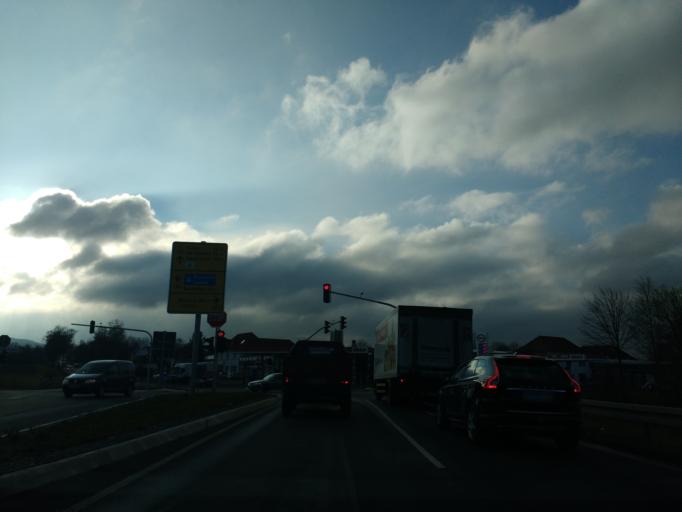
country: DE
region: Hesse
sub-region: Regierungsbezirk Giessen
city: Alsfeld
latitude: 50.7526
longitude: 9.2861
